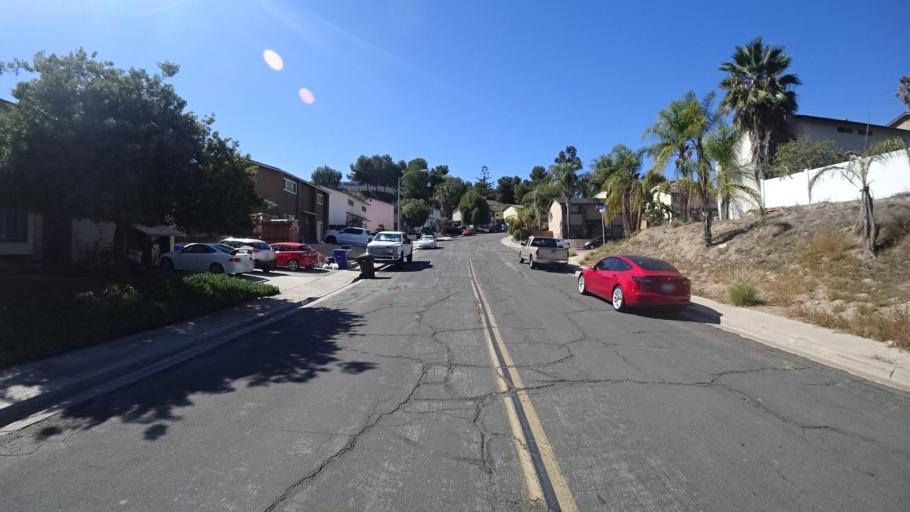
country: US
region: California
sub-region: San Diego County
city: Lemon Grove
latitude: 32.7167
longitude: -117.0231
